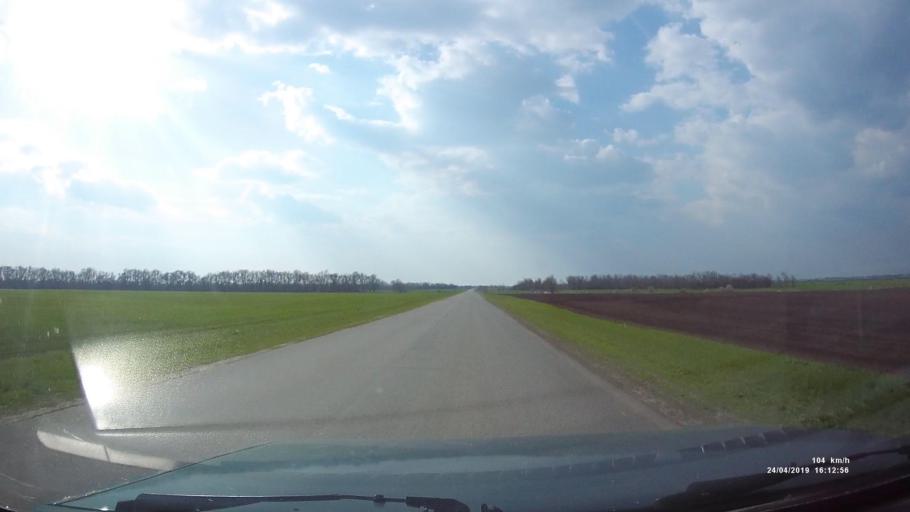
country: RU
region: Rostov
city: Sovetskoye
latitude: 46.7369
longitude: 42.2282
